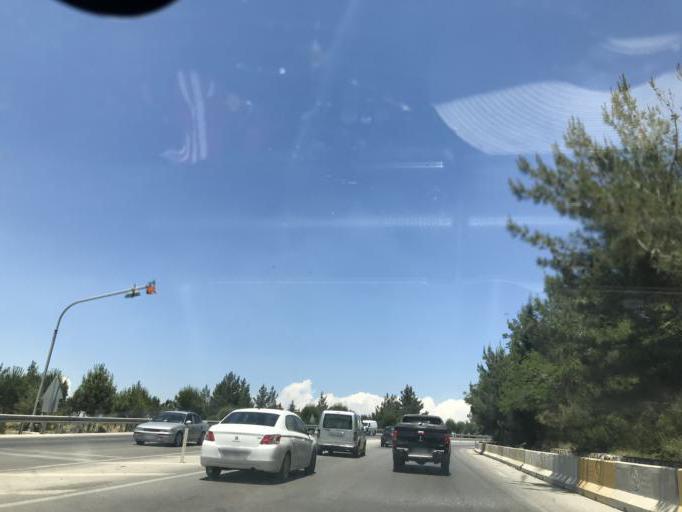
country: TR
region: Denizli
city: Denizli
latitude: 37.7301
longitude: 29.1718
